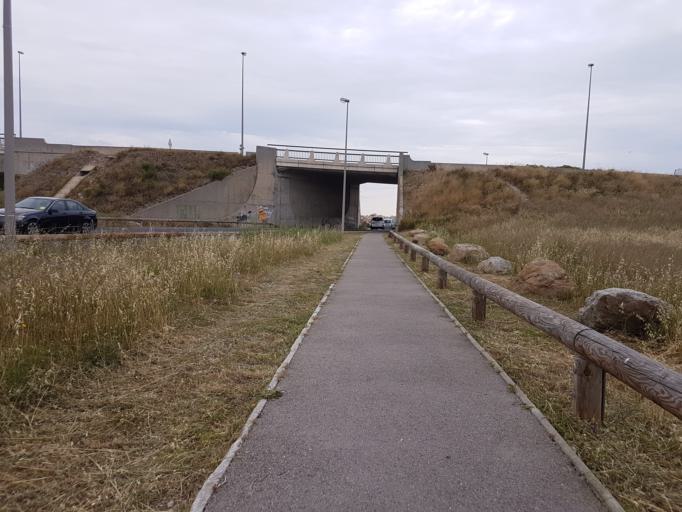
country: FR
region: Languedoc-Roussillon
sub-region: Departement de l'Herault
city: Frontignan
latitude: 43.4362
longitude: 3.7623
